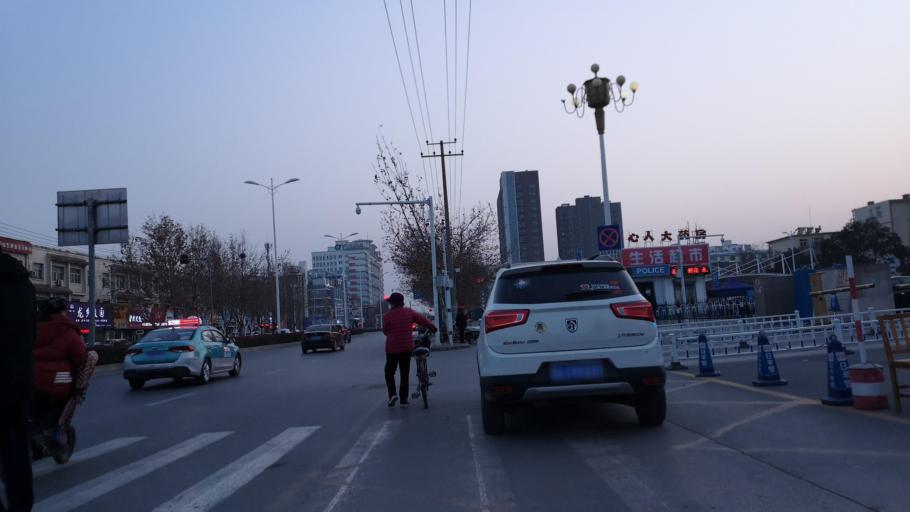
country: CN
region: Henan Sheng
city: Zhongyuanlu
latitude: 35.7710
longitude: 115.0694
